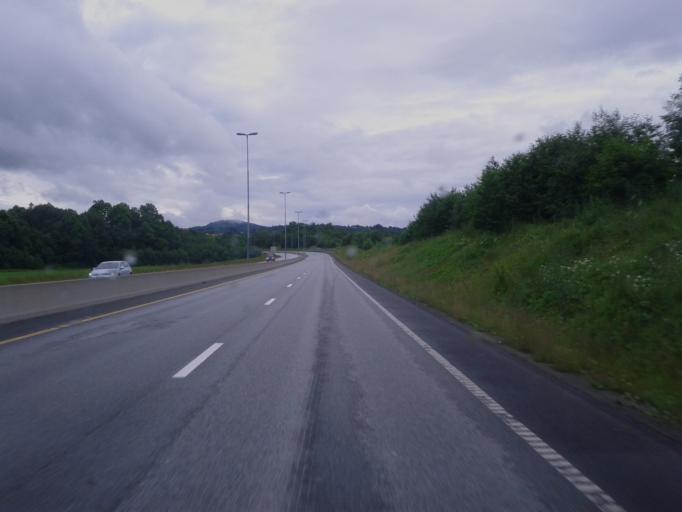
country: NO
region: Sor-Trondelag
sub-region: Melhus
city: Melhus
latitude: 63.2947
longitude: 10.2778
